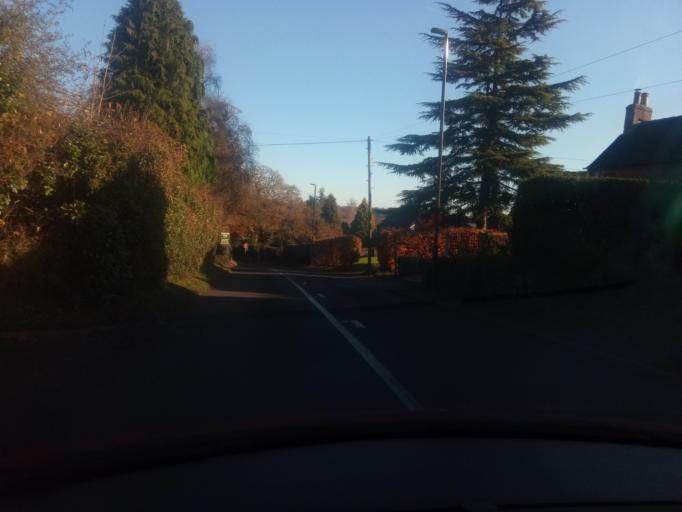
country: GB
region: England
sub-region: Derbyshire
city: Wirksworth
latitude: 53.0166
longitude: -1.5525
